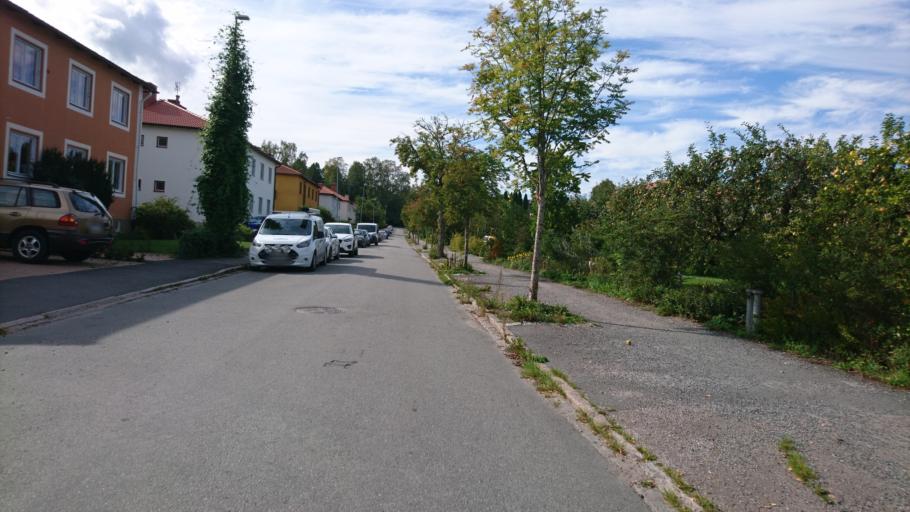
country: SE
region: Uppsala
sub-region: Uppsala Kommun
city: Uppsala
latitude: 59.8455
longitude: 17.6293
